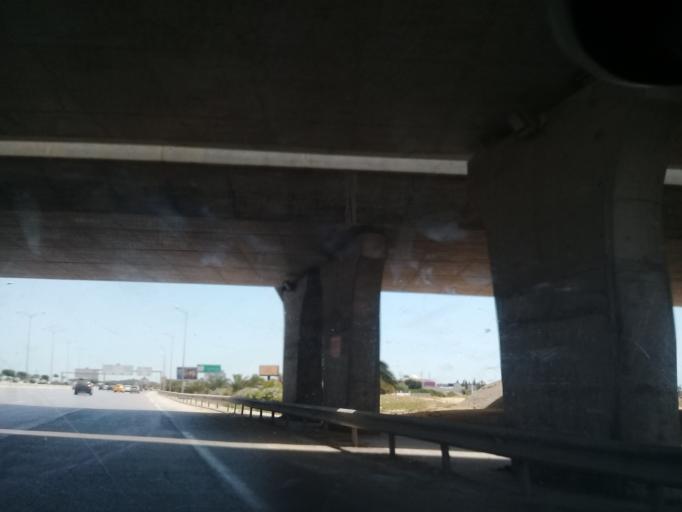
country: TN
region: Ariana
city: Ariana
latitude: 36.8312
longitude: 10.2121
